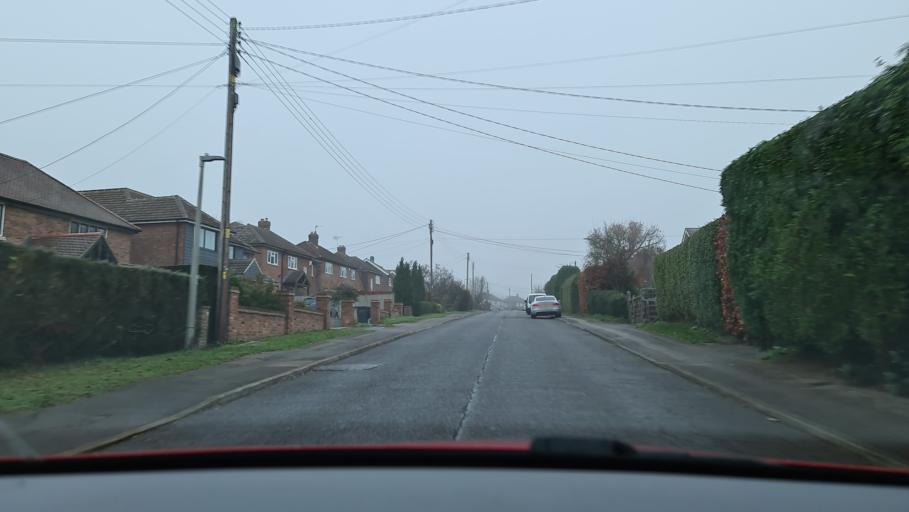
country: GB
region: England
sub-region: Buckinghamshire
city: Amersham on the Hill
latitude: 51.6662
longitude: -0.6023
